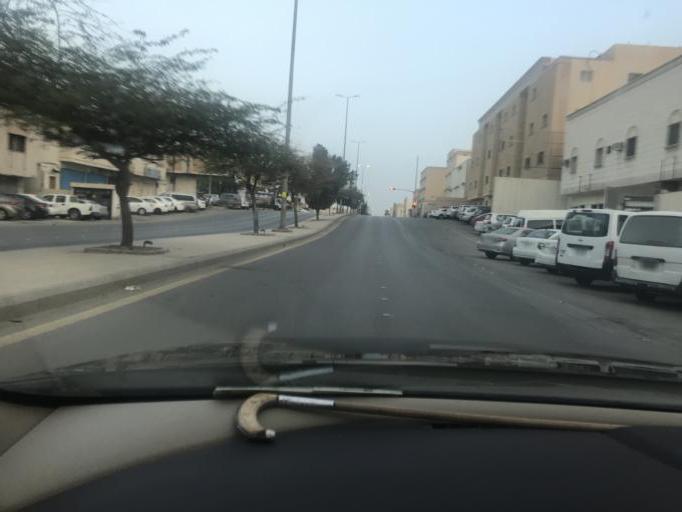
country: SA
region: Ar Riyad
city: Riyadh
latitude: 24.7286
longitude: 46.7640
